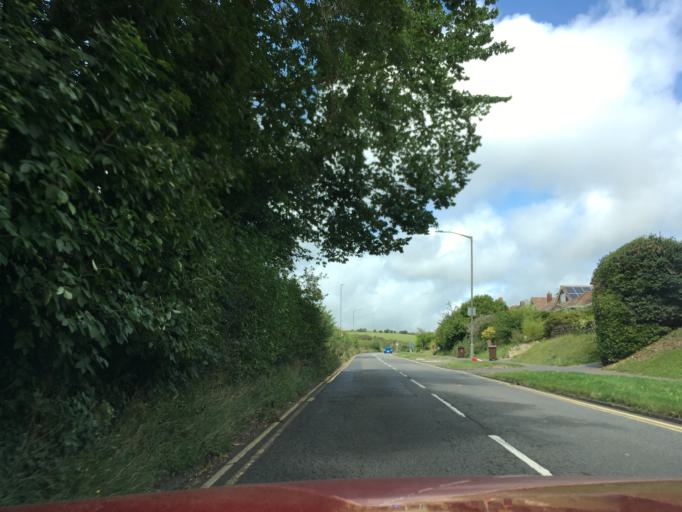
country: GB
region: England
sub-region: Brighton and Hove
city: Rottingdean
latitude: 50.8269
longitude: -0.0710
